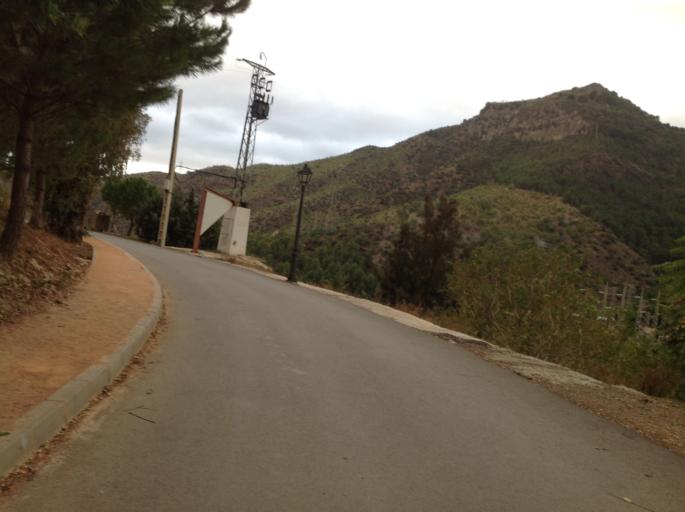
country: ES
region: Andalusia
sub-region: Provincia de Malaga
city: Carratraca
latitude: 36.9100
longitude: -4.7612
